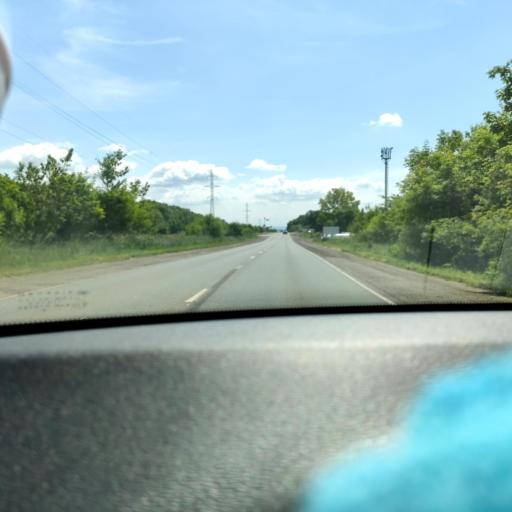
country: RU
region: Samara
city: Novosemeykino
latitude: 53.3343
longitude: 50.2538
